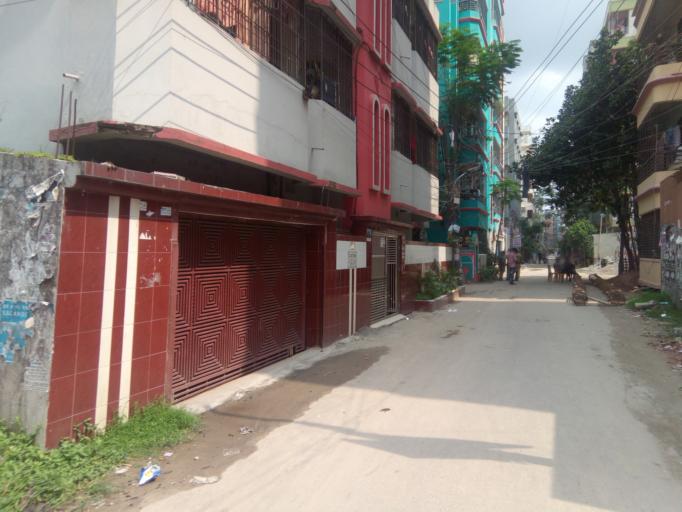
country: BD
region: Dhaka
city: Paltan
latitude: 23.7536
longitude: 90.4418
